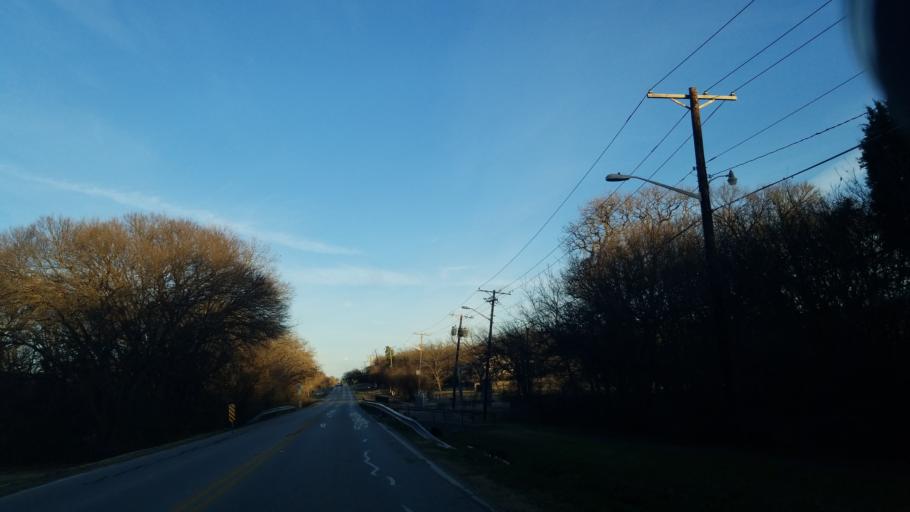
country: US
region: Texas
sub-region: Denton County
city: Denton
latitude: 33.1760
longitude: -97.1274
